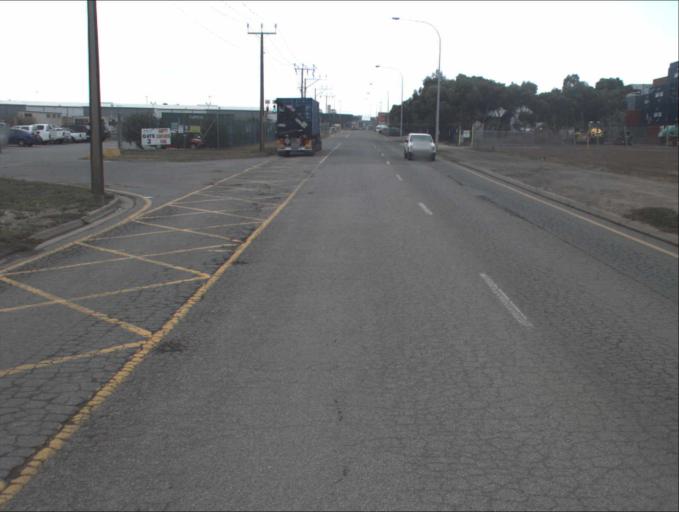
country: AU
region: South Australia
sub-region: Port Adelaide Enfield
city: Birkenhead
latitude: -34.7742
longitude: 138.4926
